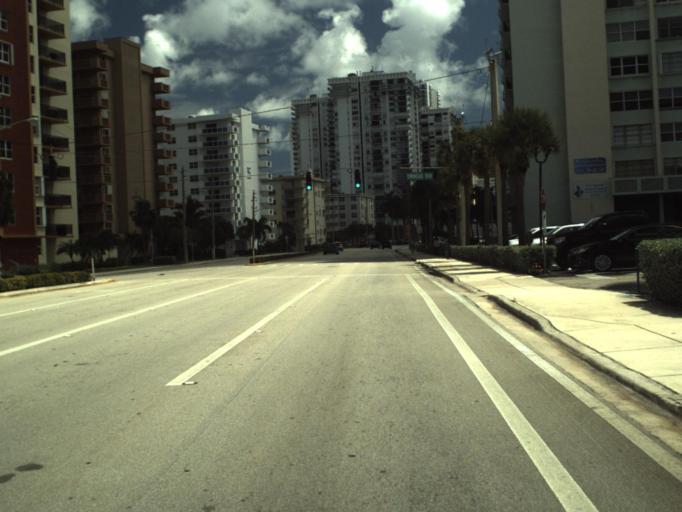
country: US
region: Florida
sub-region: Broward County
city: Hollywood
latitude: 26.0036
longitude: -80.1183
